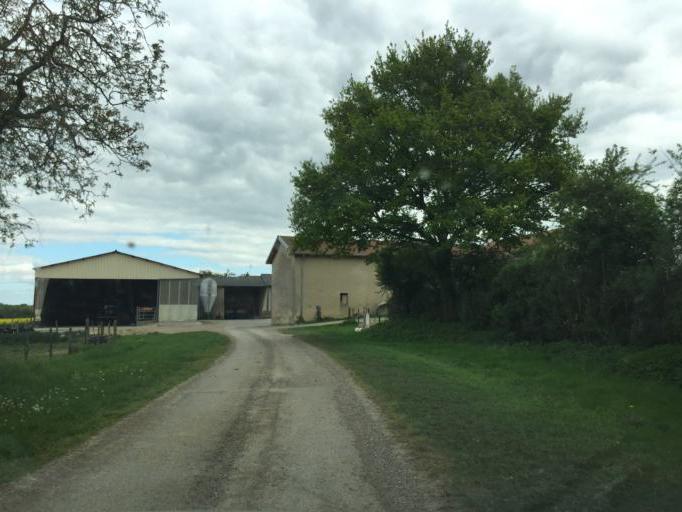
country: FR
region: Rhone-Alpes
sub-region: Departement de l'Ain
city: Tramoyes
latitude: 45.8935
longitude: 4.9767
